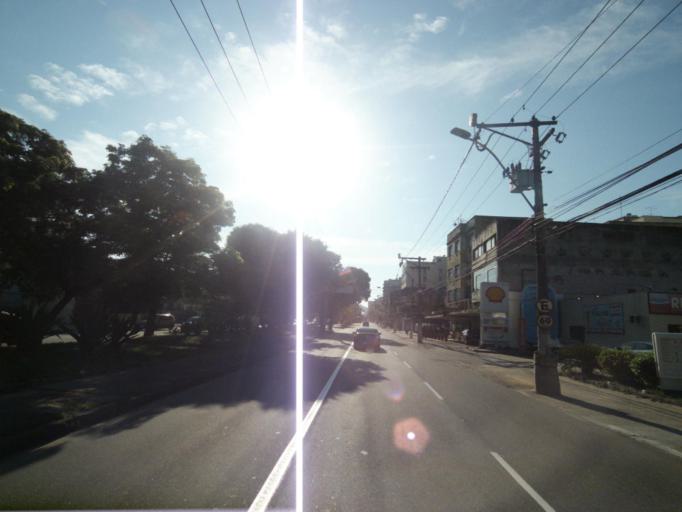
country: BR
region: Rio de Janeiro
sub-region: Niteroi
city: Niteroi
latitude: -22.8807
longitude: -43.1056
